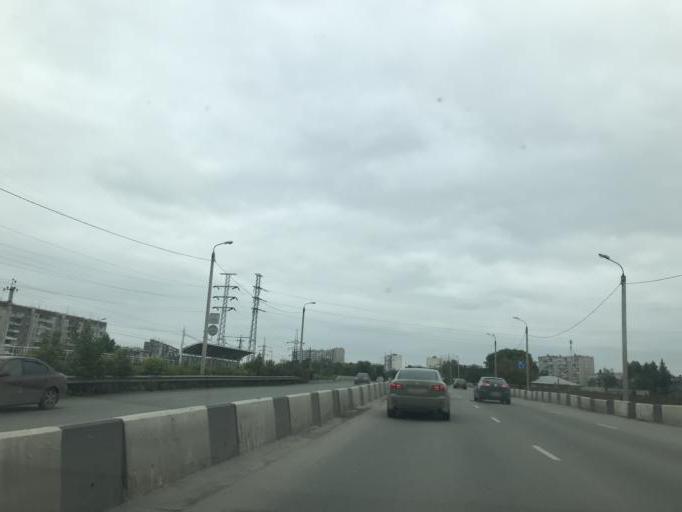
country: RU
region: Chelyabinsk
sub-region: Gorod Chelyabinsk
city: Chelyabinsk
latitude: 55.1668
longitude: 61.4286
